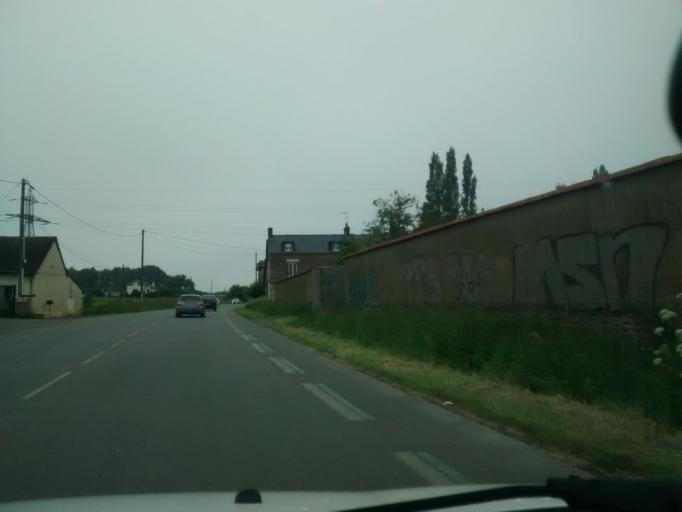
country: FR
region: Brittany
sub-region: Departement d'Ille-et-Vilaine
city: Saint-Gregoire
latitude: 48.1417
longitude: -1.7012
